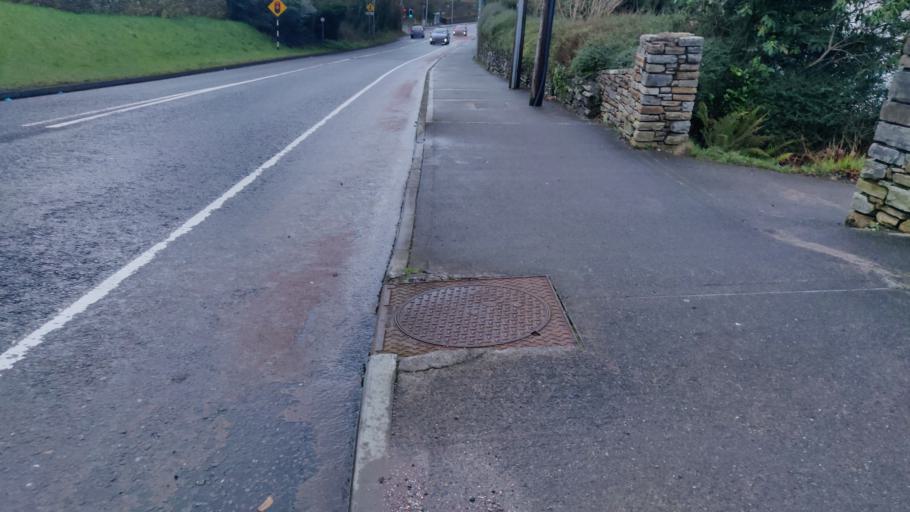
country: IE
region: Munster
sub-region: County Cork
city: Cork
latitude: 51.8721
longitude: -8.4206
